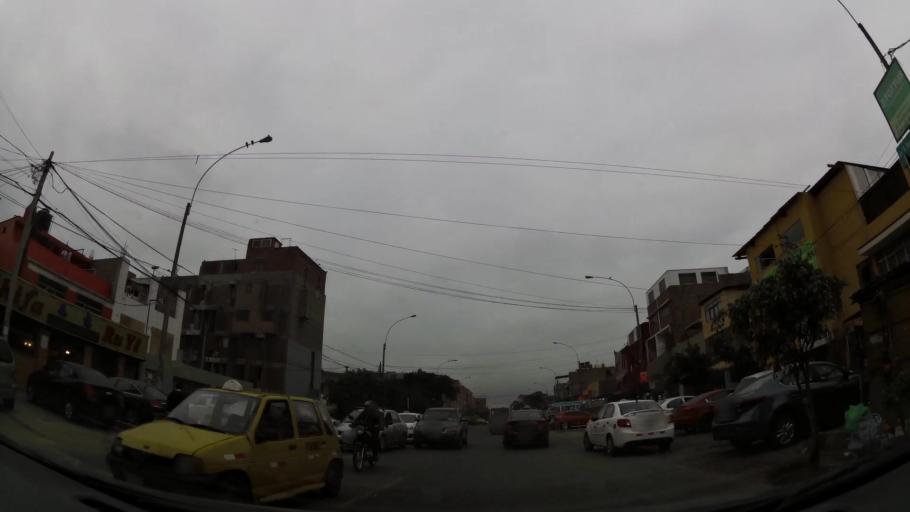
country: PE
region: Lima
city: Lima
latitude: -12.0546
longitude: -77.0691
